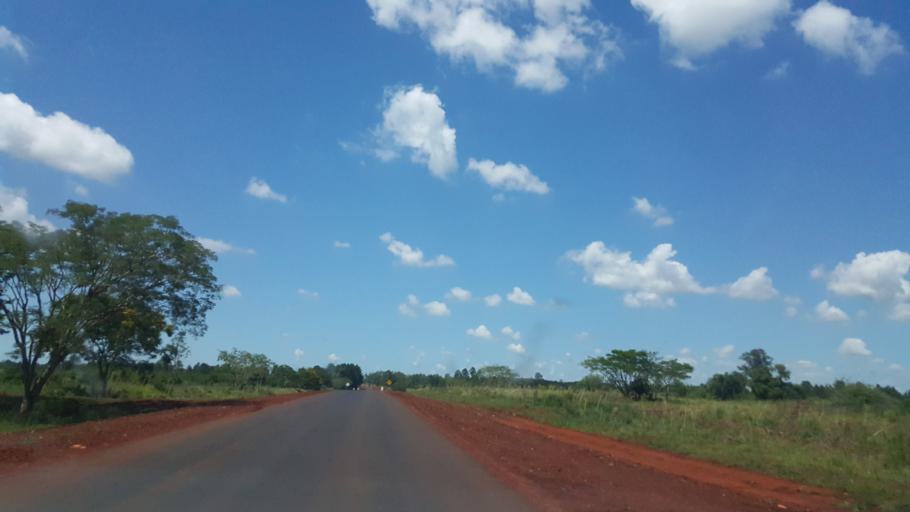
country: AR
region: Corrientes
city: Santo Tome
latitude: -28.4990
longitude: -56.0519
